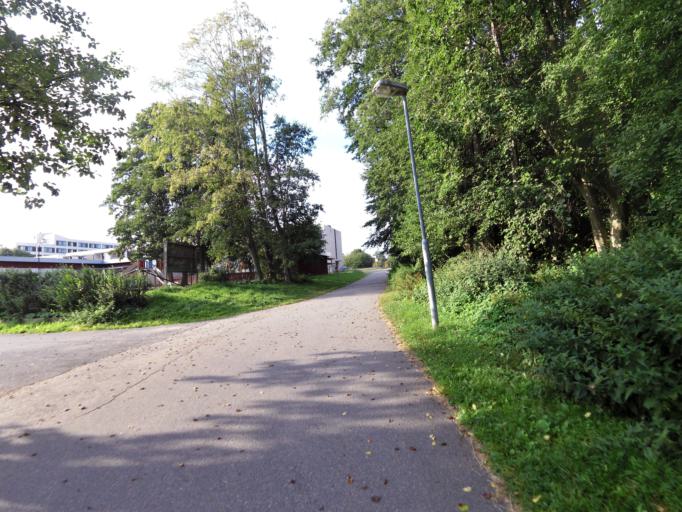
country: SE
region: Gaevleborg
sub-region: Gavle Kommun
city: Gavle
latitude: 60.6903
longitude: 17.1187
